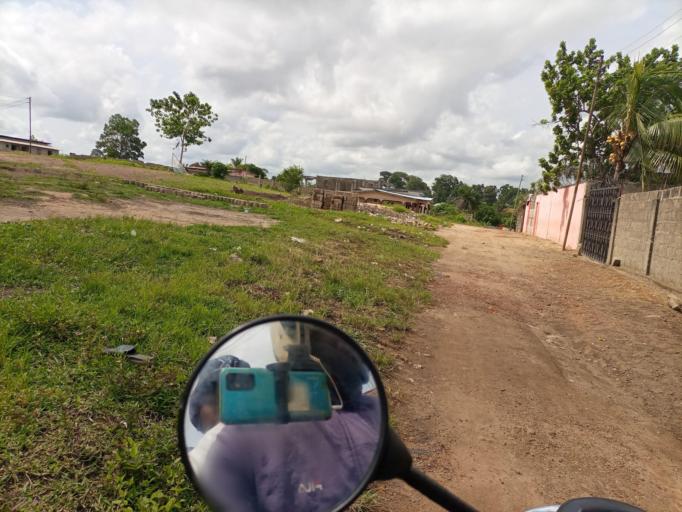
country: SL
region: Southern Province
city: Bo
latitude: 7.9728
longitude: -11.7577
